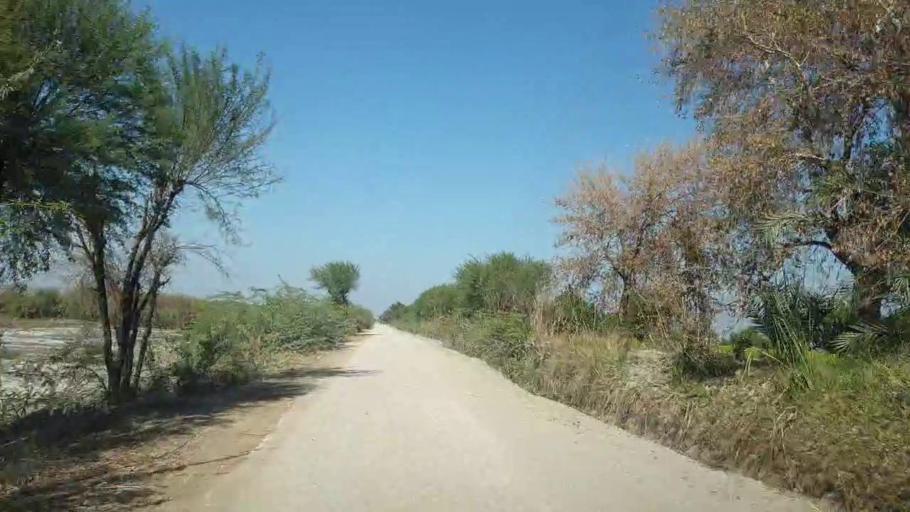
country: PK
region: Sindh
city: Mirpur Khas
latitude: 25.6555
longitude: 69.0272
